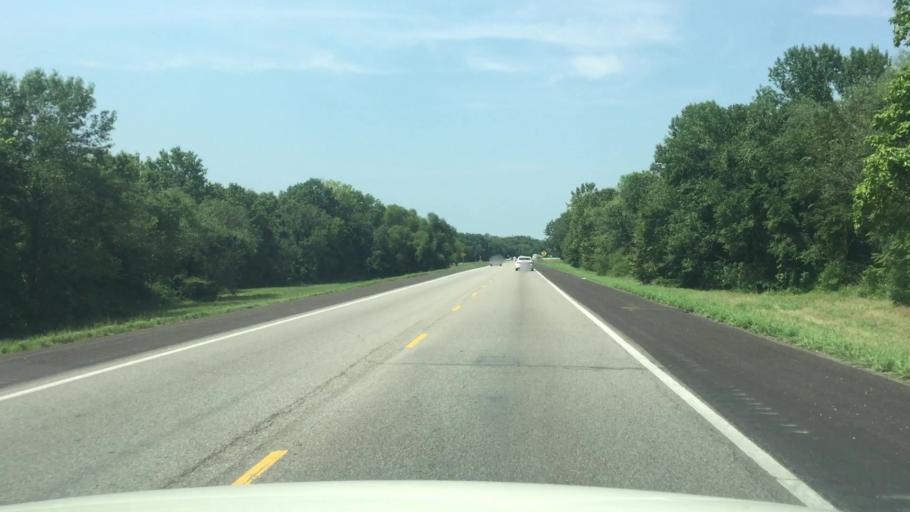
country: US
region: Kansas
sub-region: Crawford County
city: Pittsburg
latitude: 37.4018
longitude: -94.7219
